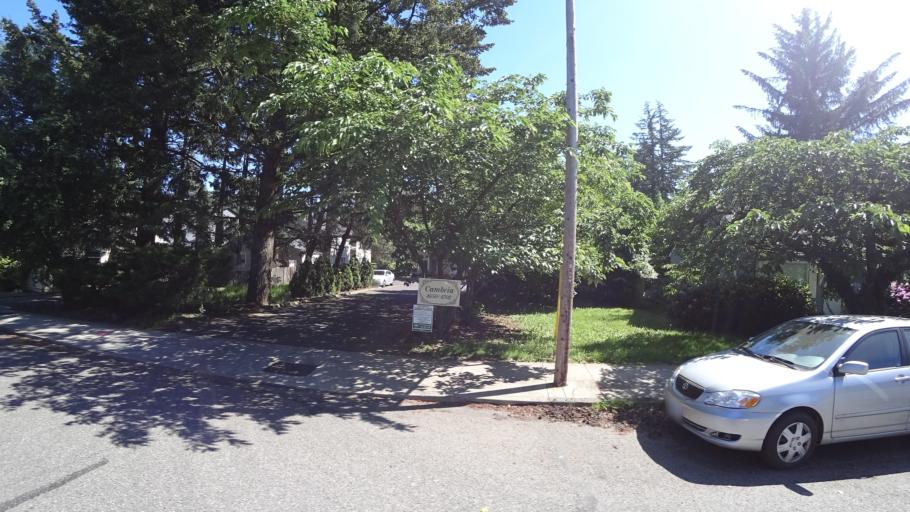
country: US
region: Oregon
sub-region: Washington County
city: Metzger
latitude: 45.4507
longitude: -122.7255
